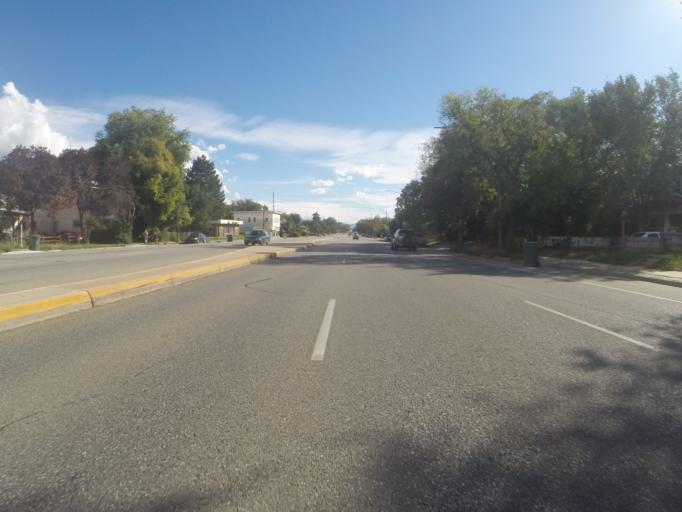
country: US
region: Utah
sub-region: Salt Lake County
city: Salt Lake City
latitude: 40.7556
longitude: -111.8711
